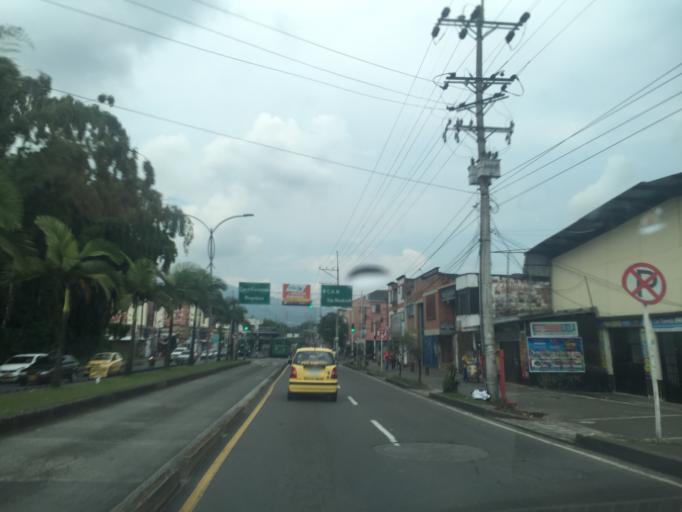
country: CO
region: Risaralda
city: Pereira
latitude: 4.8256
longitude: -75.6822
